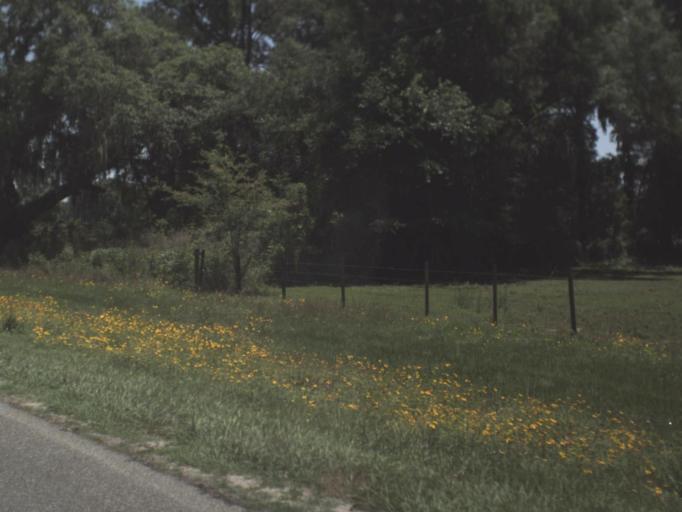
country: US
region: Florida
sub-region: Suwannee County
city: Wellborn
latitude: 30.2487
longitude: -82.8852
